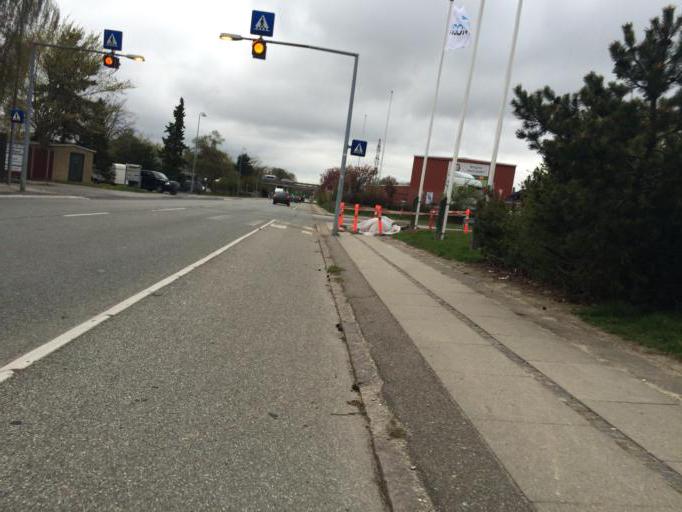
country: DK
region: Capital Region
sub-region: Vallensbaek Kommune
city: Vallensbaek
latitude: 55.6254
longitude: 12.3734
